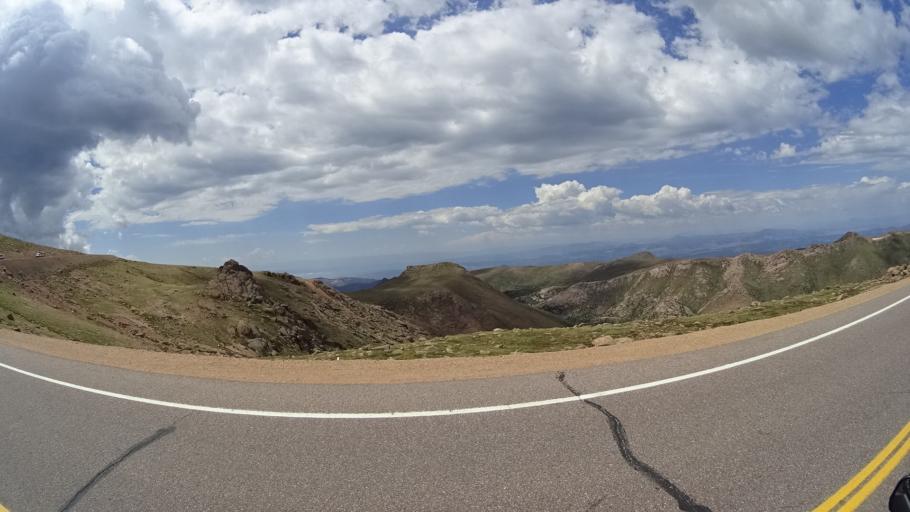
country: US
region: Colorado
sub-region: El Paso County
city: Cascade-Chipita Park
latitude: 38.8524
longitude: -105.0622
